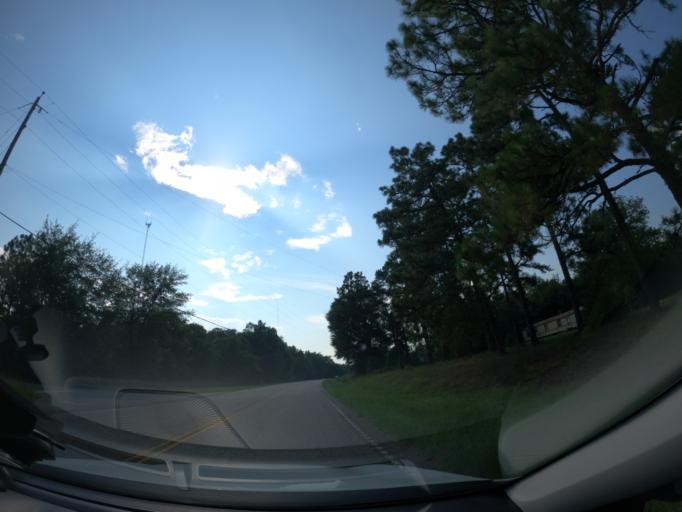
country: US
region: South Carolina
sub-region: Aiken County
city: Jackson
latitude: 33.4085
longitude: -81.8256
